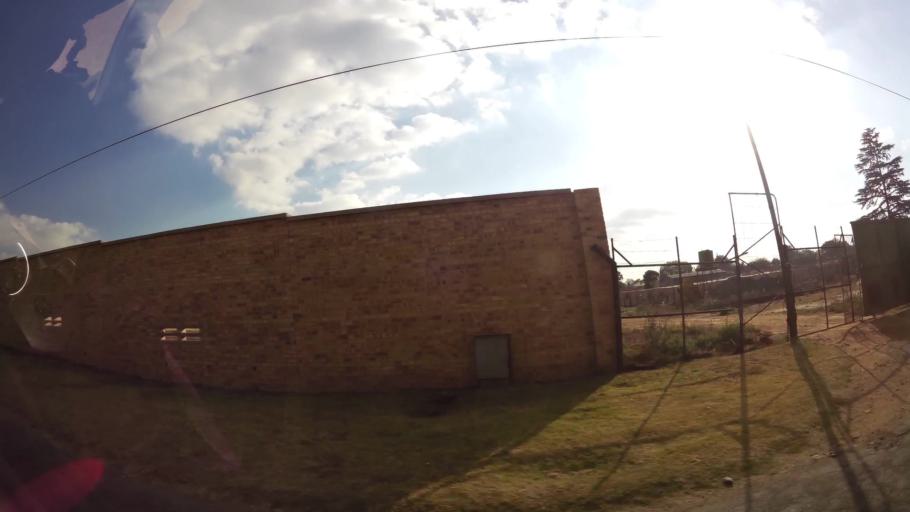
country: ZA
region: Gauteng
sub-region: West Rand District Municipality
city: Krugersdorp
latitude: -26.0901
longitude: 27.7446
